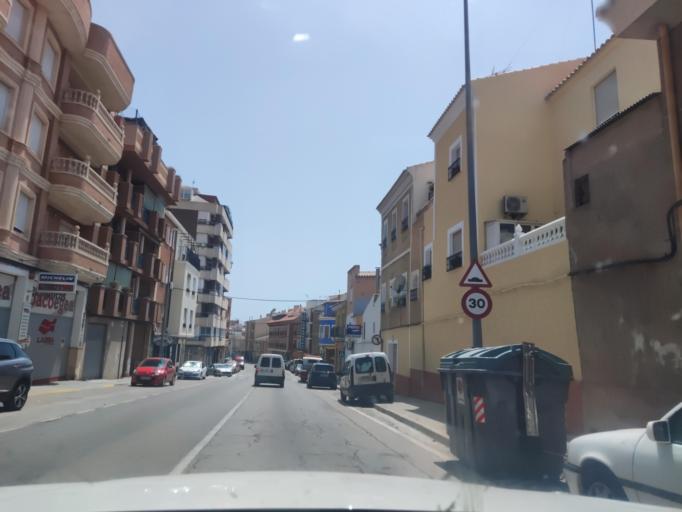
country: ES
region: Castille-La Mancha
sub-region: Provincia de Albacete
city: Hellin
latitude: 38.5135
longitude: -1.6973
